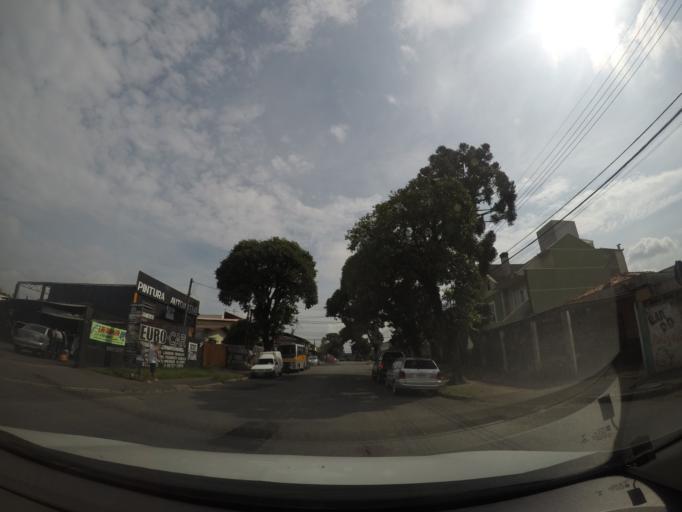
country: BR
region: Parana
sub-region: Sao Jose Dos Pinhais
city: Sao Jose dos Pinhais
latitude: -25.5105
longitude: -49.2833
